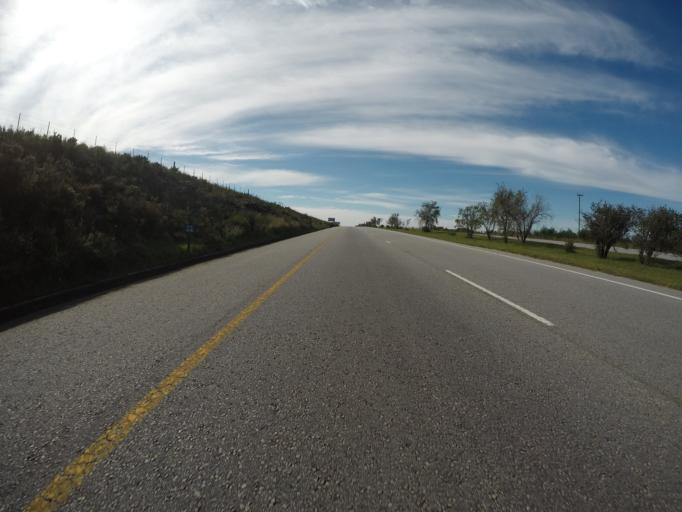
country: ZA
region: Eastern Cape
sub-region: Nelson Mandela Bay Metropolitan Municipality
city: Uitenhage
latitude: -33.9105
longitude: 25.2029
